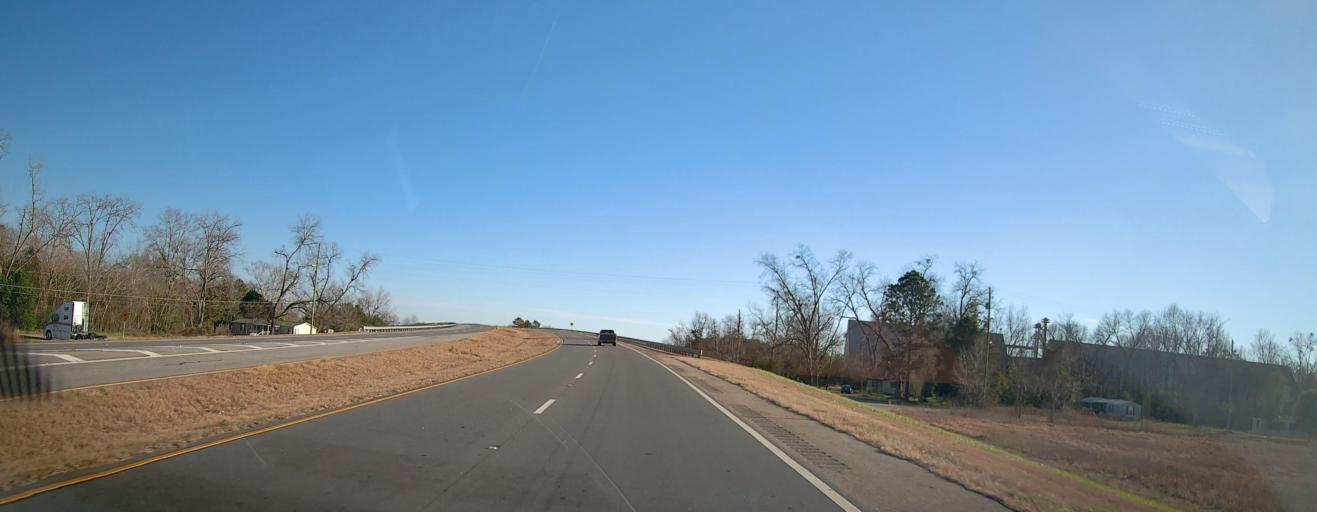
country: US
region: Georgia
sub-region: Sumter County
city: Americus
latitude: 31.8994
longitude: -84.2625
